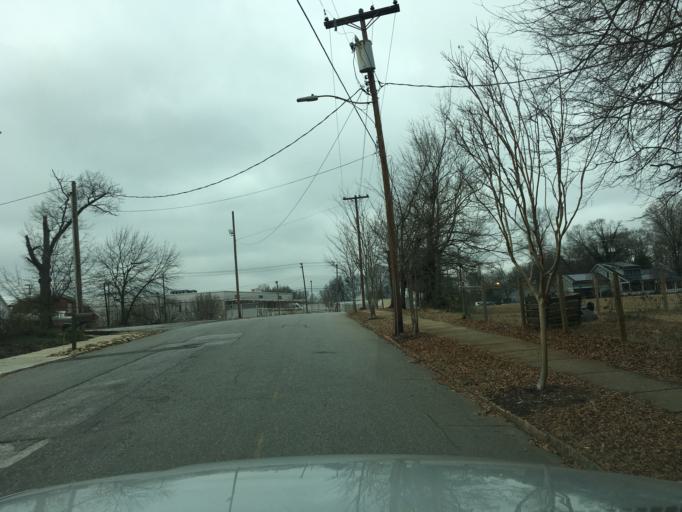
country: US
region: South Carolina
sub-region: Greenville County
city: Greenville
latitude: 34.8543
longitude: -82.4060
